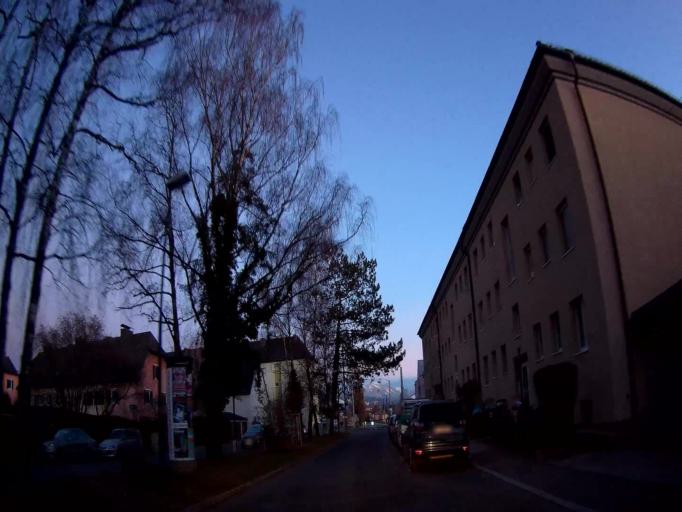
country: DE
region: Bavaria
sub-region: Upper Bavaria
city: Freilassing
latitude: 47.8080
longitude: 13.0001
